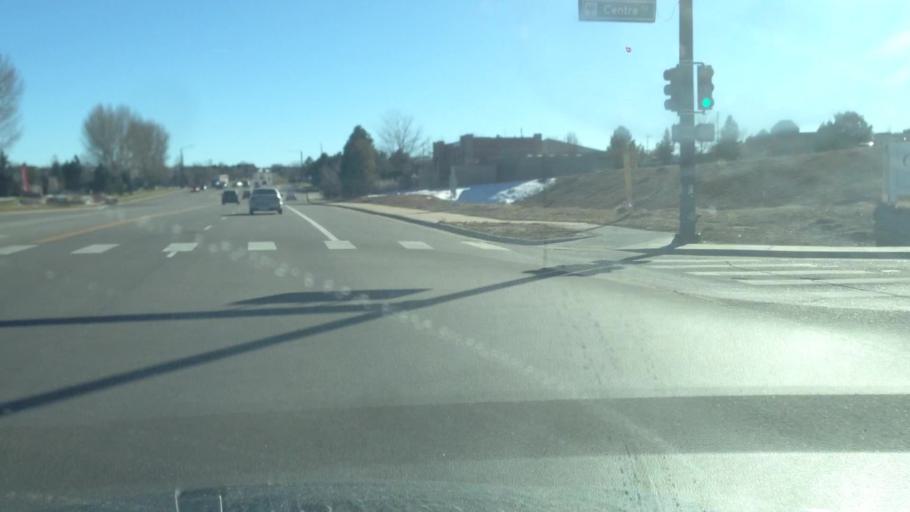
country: US
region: Colorado
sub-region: Douglas County
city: Stonegate
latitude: 39.5368
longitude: -104.7936
